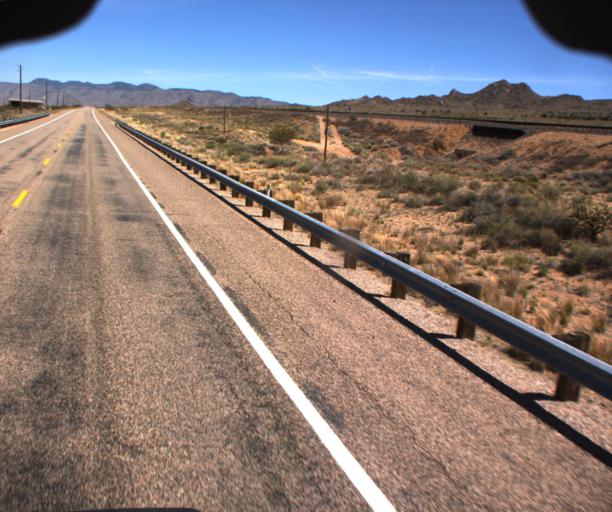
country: US
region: Arizona
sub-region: Mohave County
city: New Kingman-Butler
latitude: 35.3951
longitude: -113.8404
